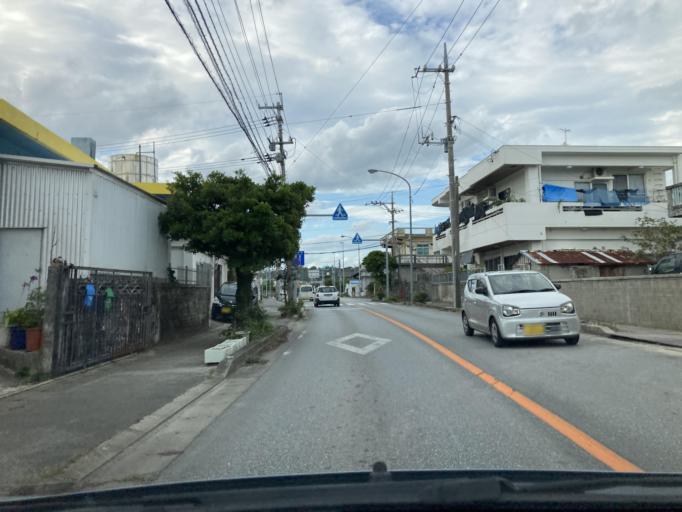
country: JP
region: Okinawa
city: Katsuren-haebaru
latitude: 26.3399
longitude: 127.8720
